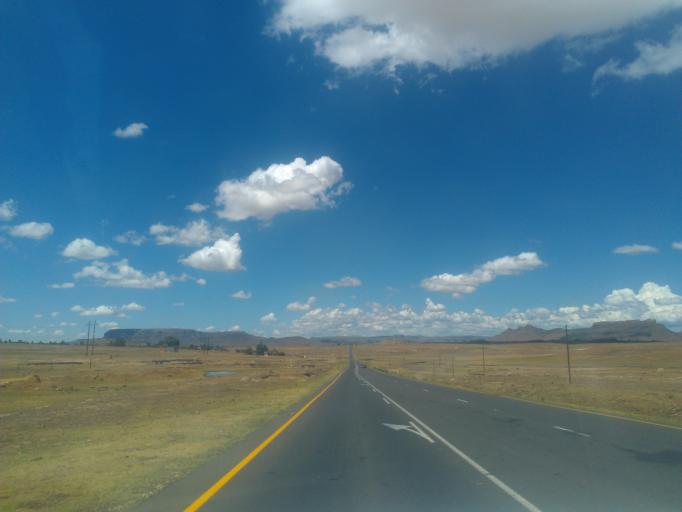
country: LS
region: Mafeteng
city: Mafeteng
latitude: -29.7700
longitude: 27.3093
